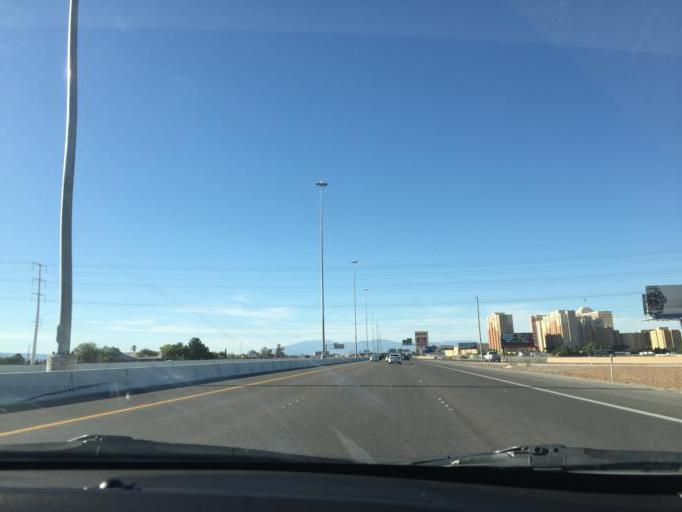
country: US
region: Nevada
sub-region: Clark County
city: Enterprise
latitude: 36.0008
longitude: -115.1805
